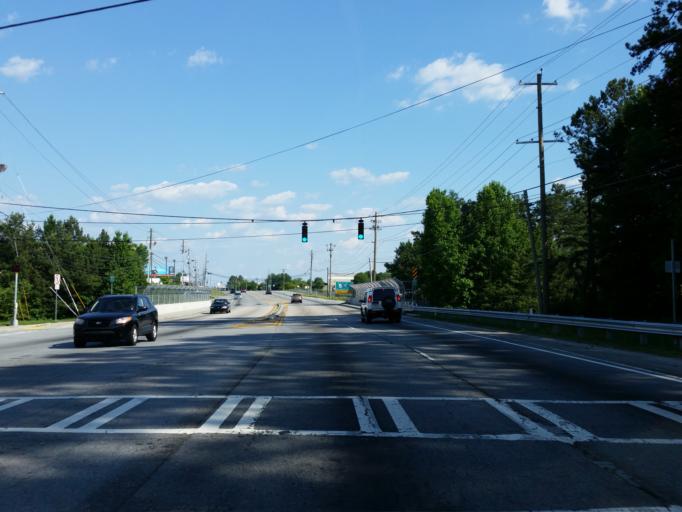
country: US
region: Georgia
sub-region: Cobb County
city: Fair Oaks
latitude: 33.9230
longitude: -84.5056
